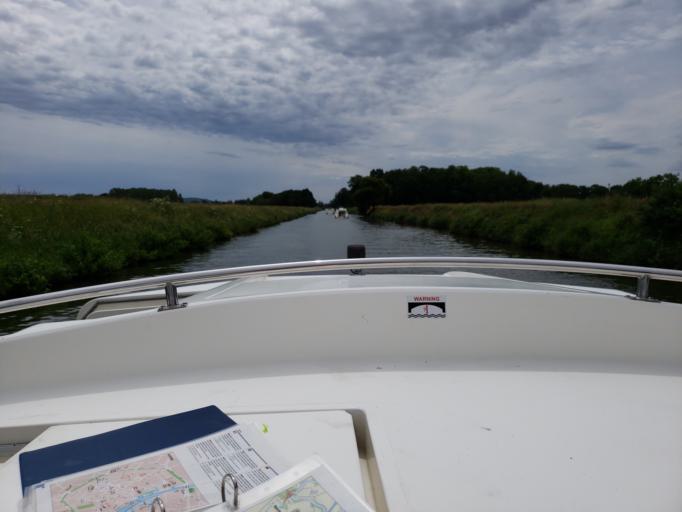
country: FR
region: Bourgogne
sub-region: Departement de l'Yonne
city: Gurgy
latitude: 47.8766
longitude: 3.5505
